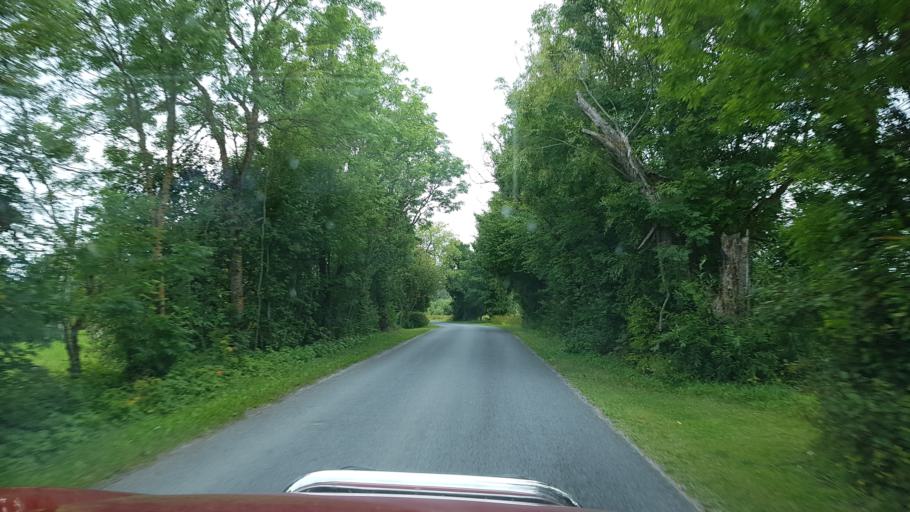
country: EE
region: Laeaene
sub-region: Ridala Parish
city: Uuemoisa
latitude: 58.8022
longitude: 23.6644
